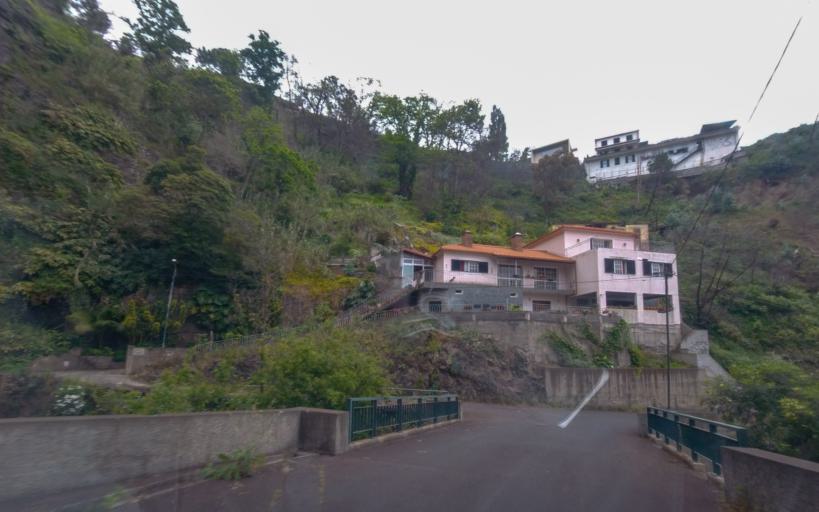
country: PT
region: Madeira
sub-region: Funchal
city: Nossa Senhora do Monte
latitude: 32.6753
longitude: -16.9116
